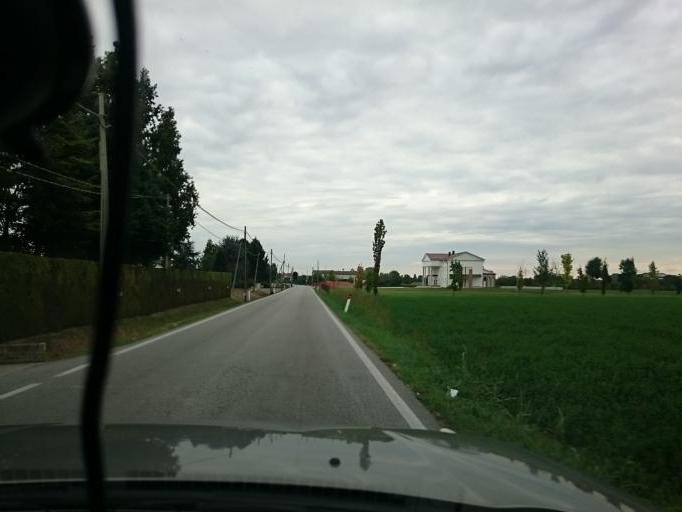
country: IT
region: Veneto
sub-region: Provincia di Padova
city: Mestrino
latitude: 45.4307
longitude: 11.7390
